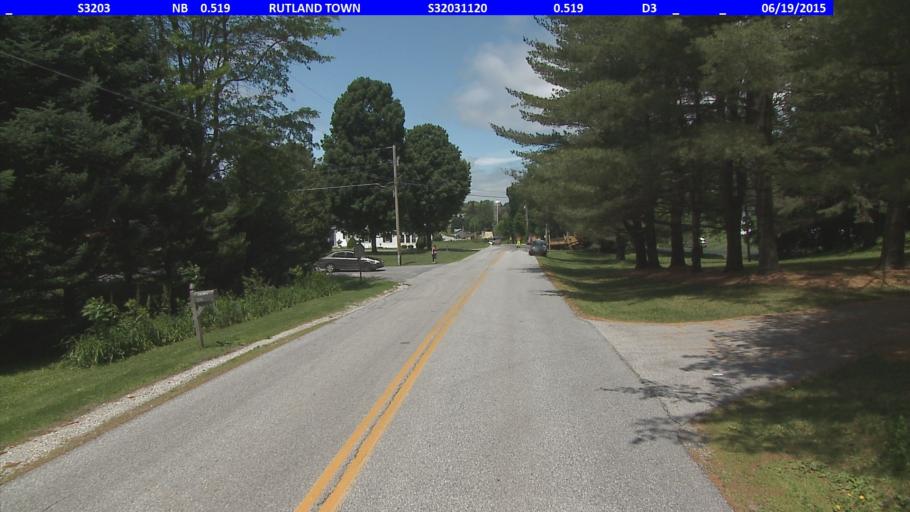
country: US
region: Vermont
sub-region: Rutland County
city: Rutland
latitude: 43.6607
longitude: -72.9988
